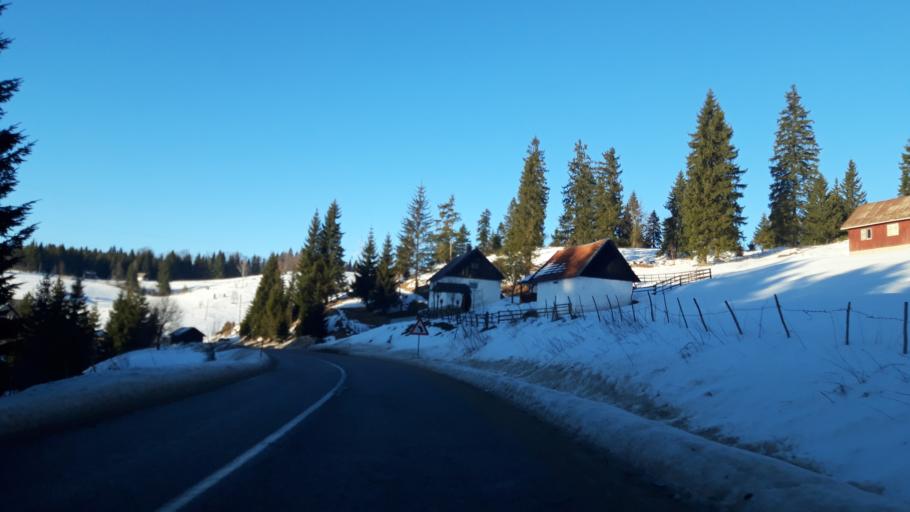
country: BA
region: Republika Srpska
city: Han Pijesak
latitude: 44.1198
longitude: 18.9694
